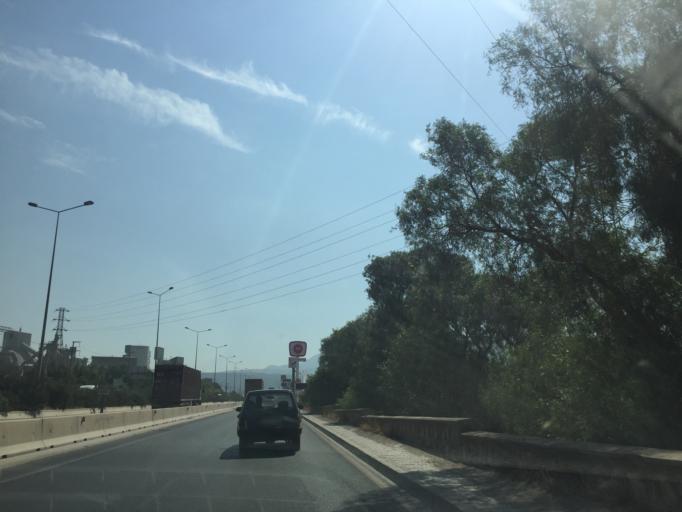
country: TR
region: Izmir
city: Bornova
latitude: 38.4553
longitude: 27.2575
